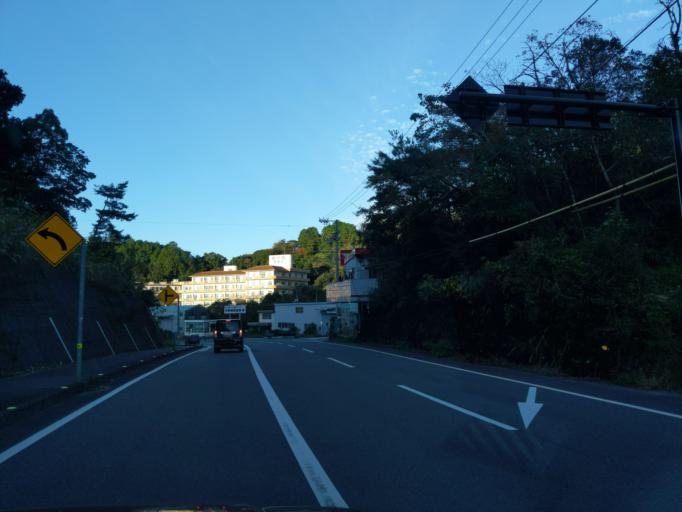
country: JP
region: Kochi
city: Muroto-misakicho
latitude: 33.5777
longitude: 134.3095
